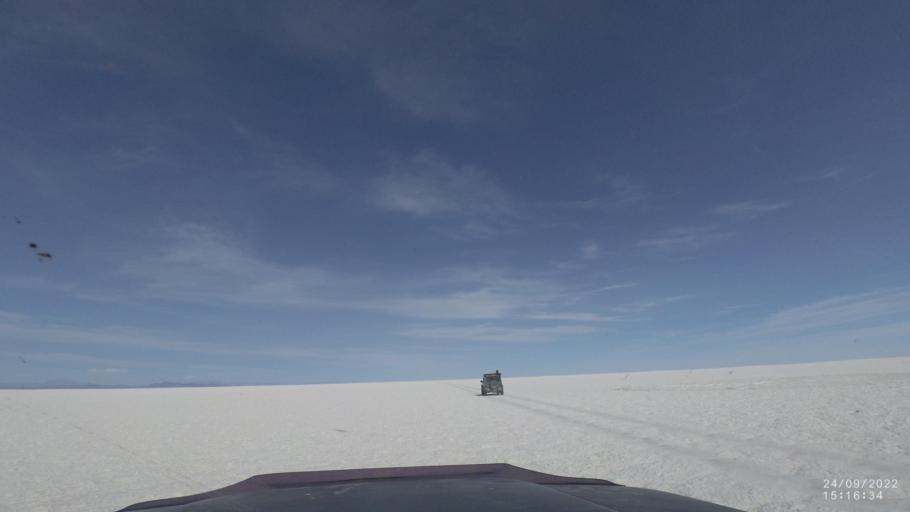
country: BO
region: Potosi
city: Colchani
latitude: -19.9827
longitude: -67.4348
